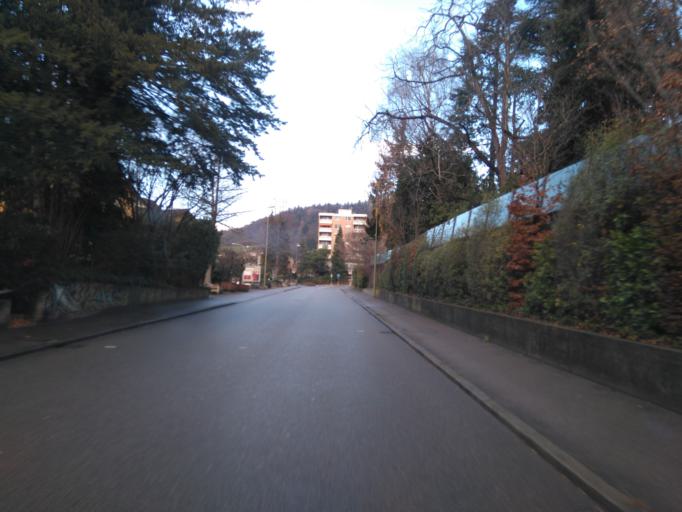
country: CH
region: Zurich
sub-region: Bezirk Dietikon
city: Unterengstringen
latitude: 47.4115
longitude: 8.4492
